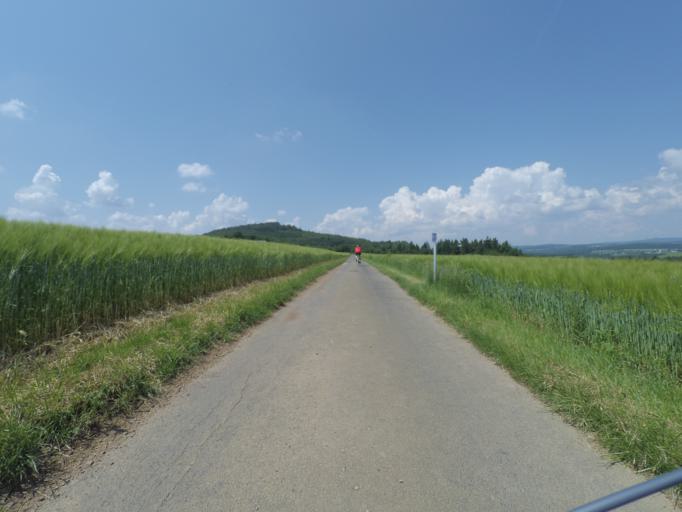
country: DE
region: Rheinland-Pfalz
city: Anschau
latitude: 50.2797
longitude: 7.1094
